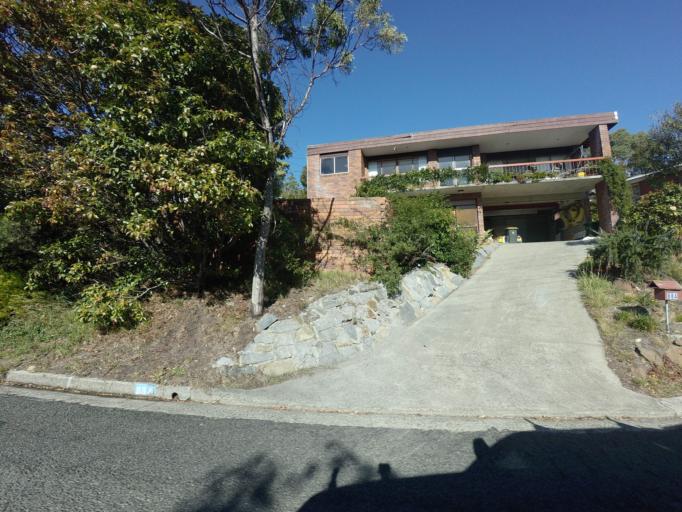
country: AU
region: Tasmania
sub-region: Clarence
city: Lindisfarne
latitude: -42.8421
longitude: 147.3411
